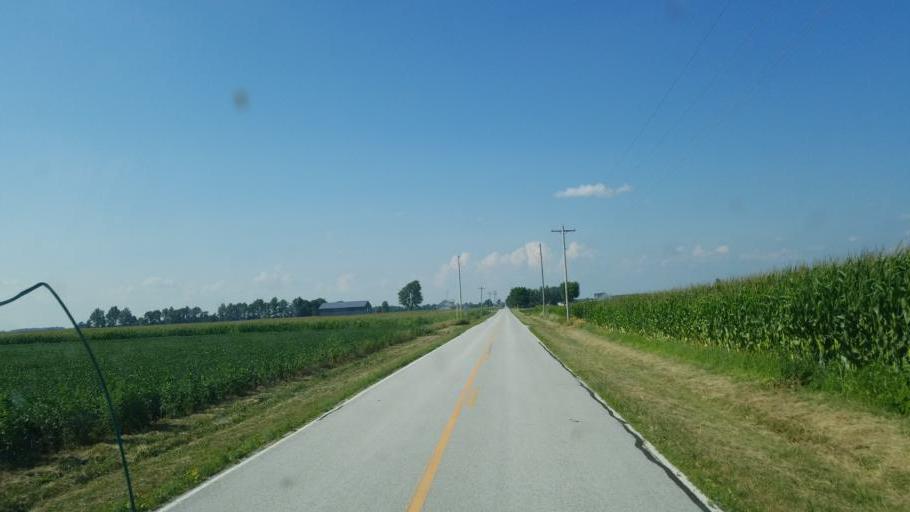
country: US
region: Ohio
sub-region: Hardin County
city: Forest
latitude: 40.7317
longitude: -83.4967
